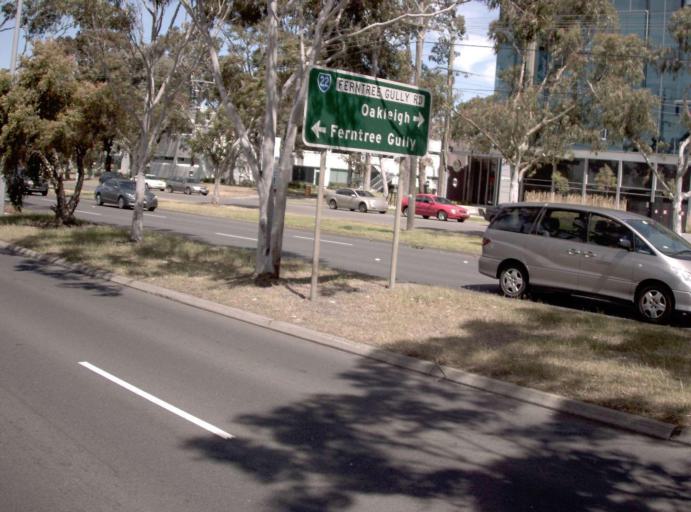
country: AU
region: Victoria
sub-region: Monash
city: Notting Hill
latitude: -37.8999
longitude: 145.1433
